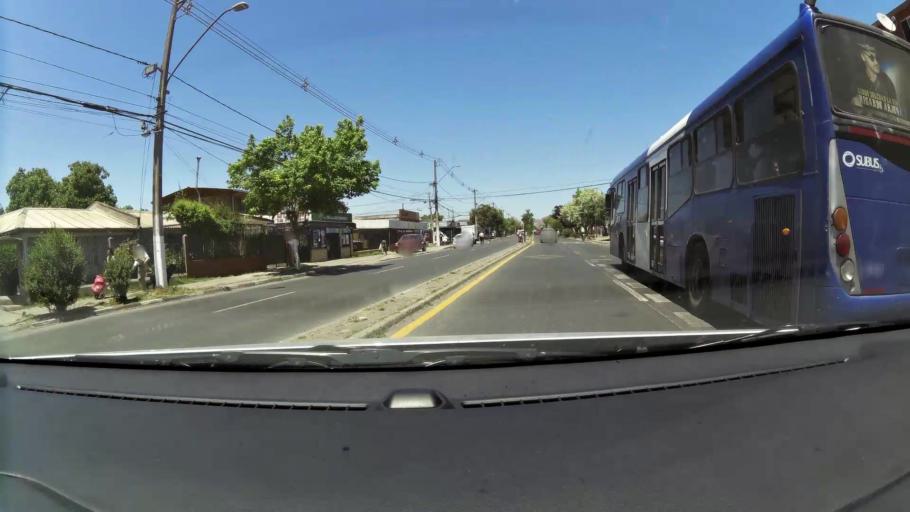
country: CL
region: Santiago Metropolitan
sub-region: Provincia de Santiago
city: La Pintana
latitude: -33.5818
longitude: -70.6624
